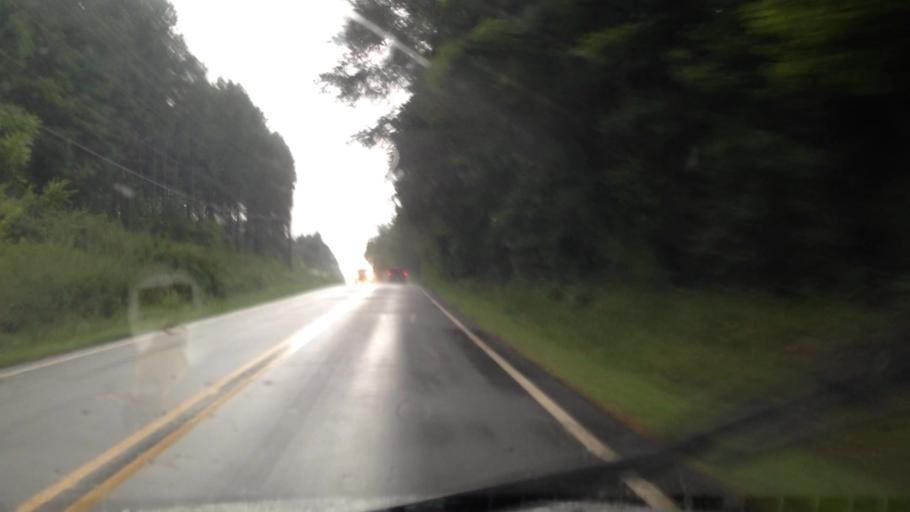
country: US
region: North Carolina
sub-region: Rockingham County
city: Reidsville
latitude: 36.2735
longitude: -79.7360
